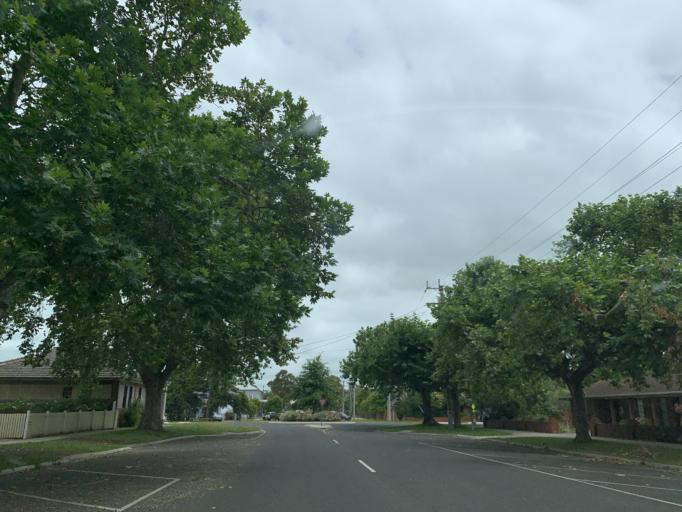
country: AU
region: Victoria
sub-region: Wellington
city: Sale
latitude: -37.9654
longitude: 146.9777
